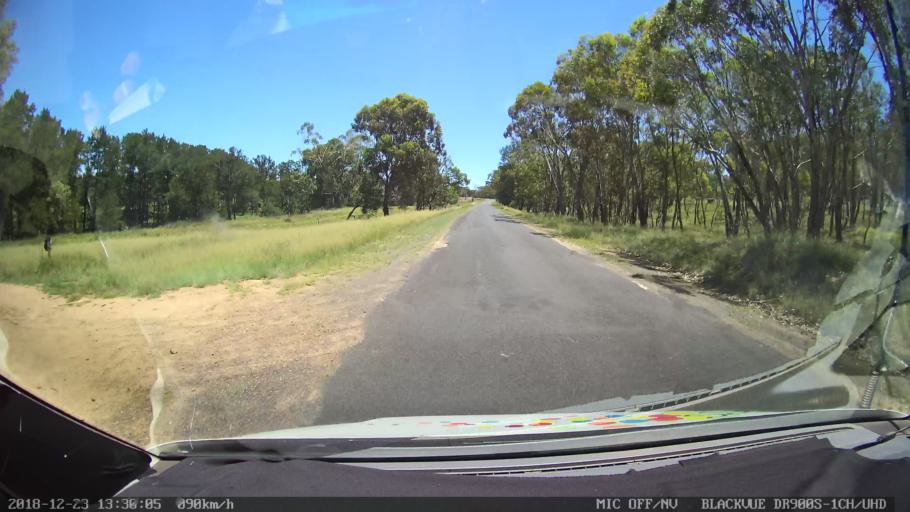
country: AU
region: New South Wales
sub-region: Armidale Dumaresq
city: Armidale
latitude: -30.4640
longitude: 151.3251
